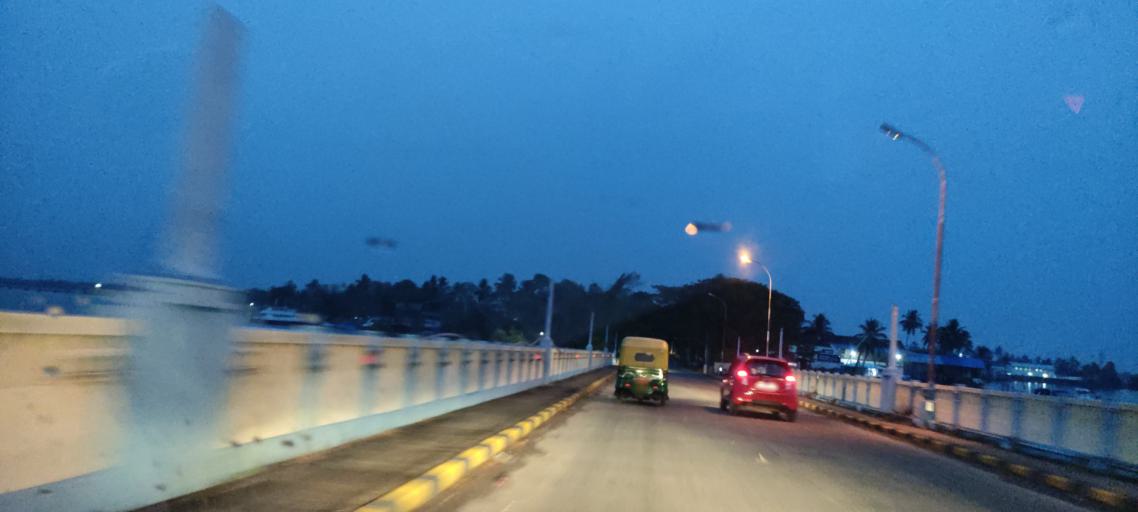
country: IN
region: Kerala
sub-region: Alappuzha
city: Arukutti
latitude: 9.8910
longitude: 76.2965
